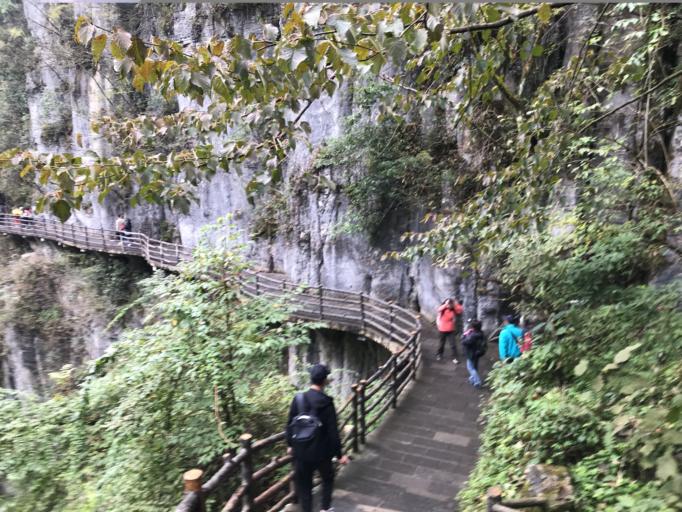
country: CN
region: Hubei
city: Tuanbao
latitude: 30.4246
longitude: 109.1665
